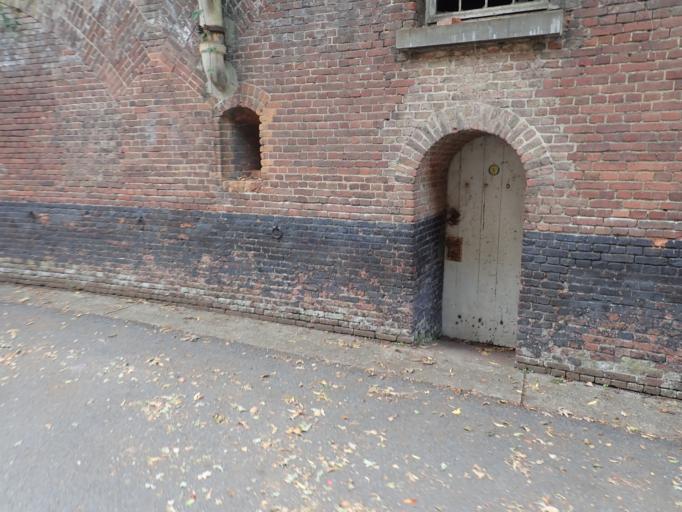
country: BE
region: Flanders
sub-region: Provincie Antwerpen
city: Borsbeek
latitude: 51.2029
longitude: 4.4918
